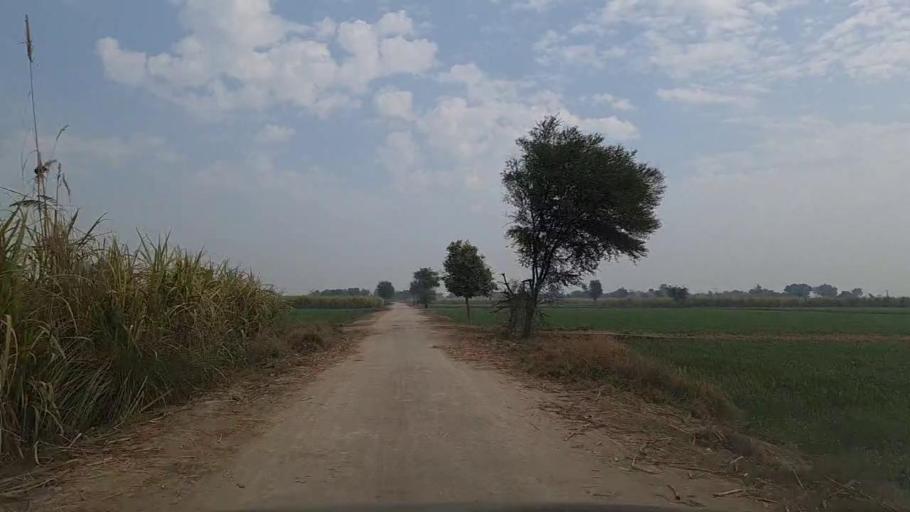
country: PK
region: Sindh
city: Daur
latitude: 26.3915
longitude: 68.3552
